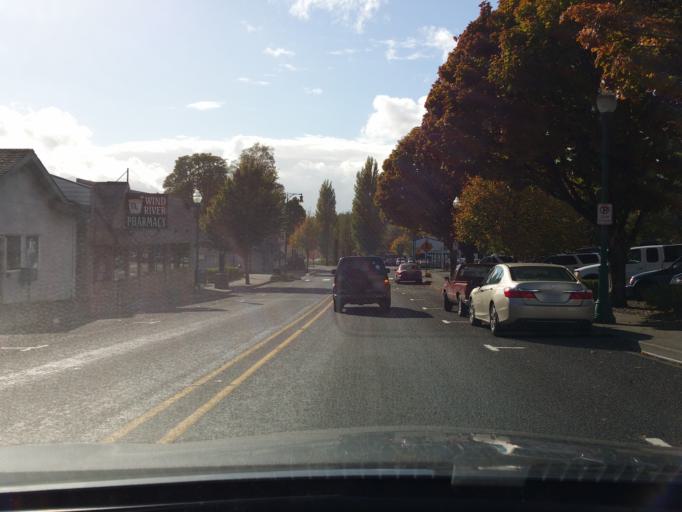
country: US
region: Washington
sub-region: Skamania County
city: Stevenson
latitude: 45.6932
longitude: -121.8847
